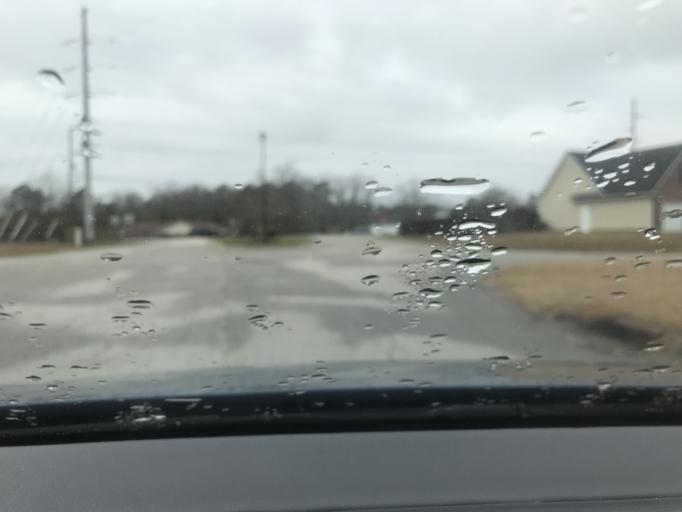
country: US
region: North Carolina
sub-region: Hoke County
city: Rockfish
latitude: 35.0197
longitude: -79.0017
